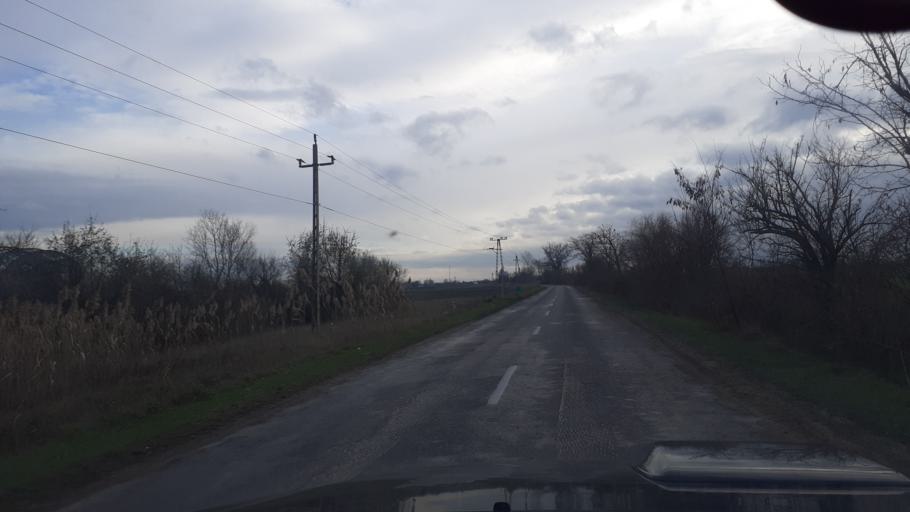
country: HU
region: Bacs-Kiskun
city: Fulopszallas
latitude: 46.8399
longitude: 19.2376
